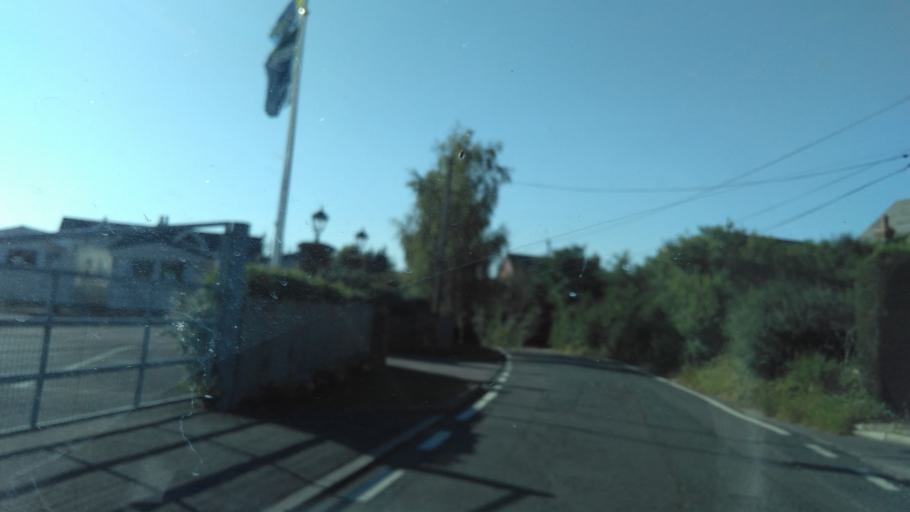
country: GB
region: England
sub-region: Kent
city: Whitstable
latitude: 51.3410
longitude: 1.0061
